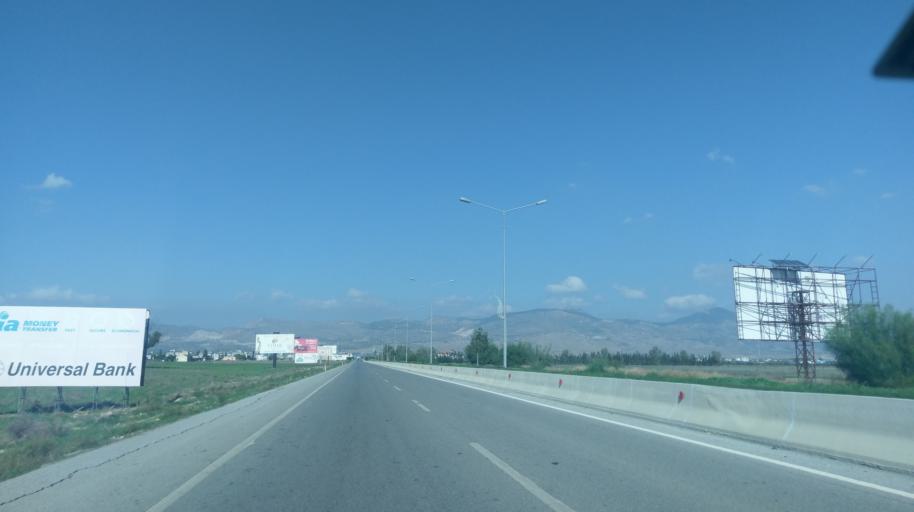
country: CY
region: Lefkosia
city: Geri
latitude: 35.1994
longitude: 33.5003
